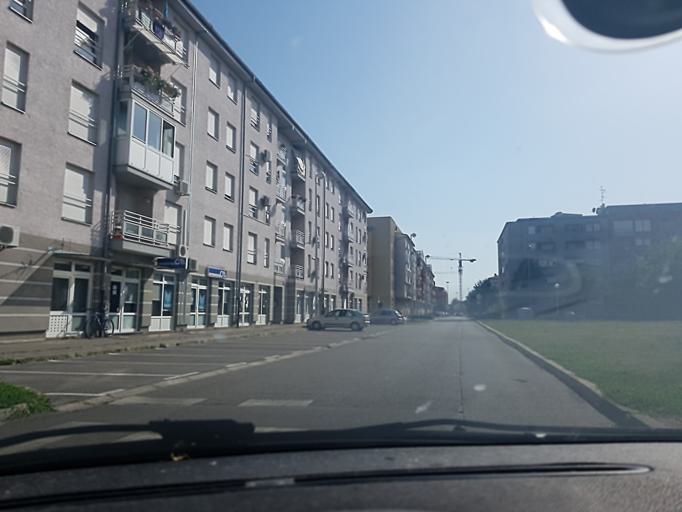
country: HR
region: Grad Zagreb
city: Jankomir
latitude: 45.7937
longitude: 15.9136
